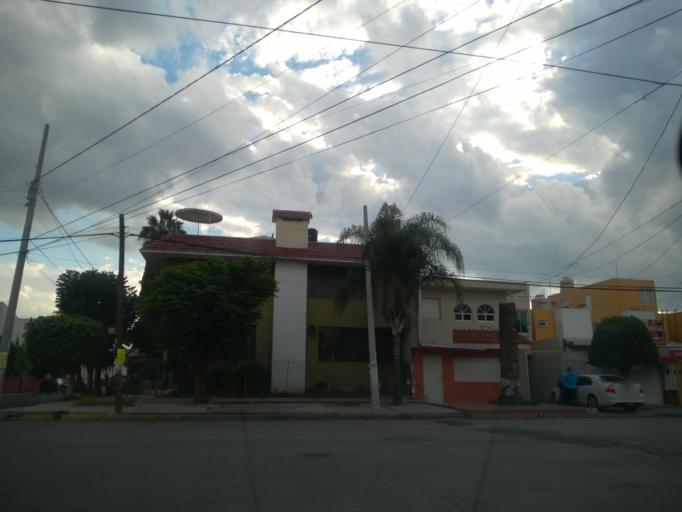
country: MX
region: Guanajuato
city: Leon
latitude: 21.1066
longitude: -101.6501
